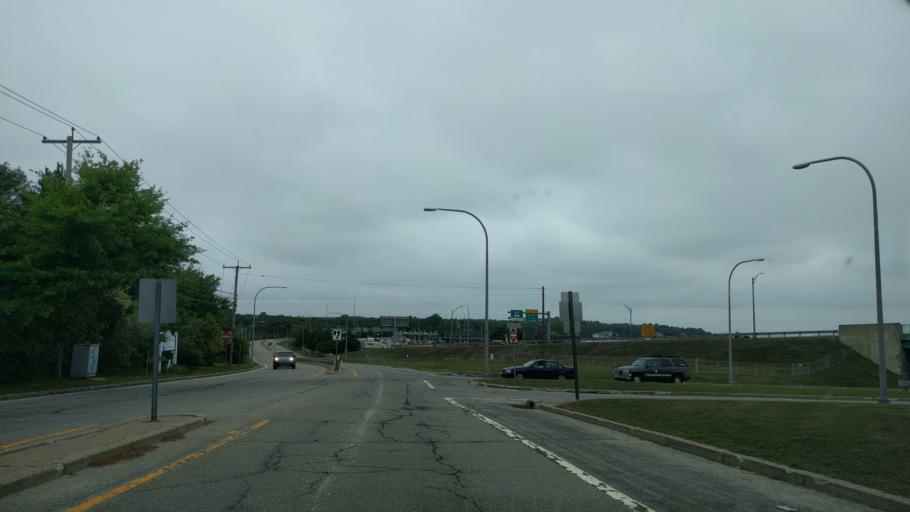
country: US
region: Rhode Island
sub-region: Newport County
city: Jamestown
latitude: 41.5079
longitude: -71.3648
